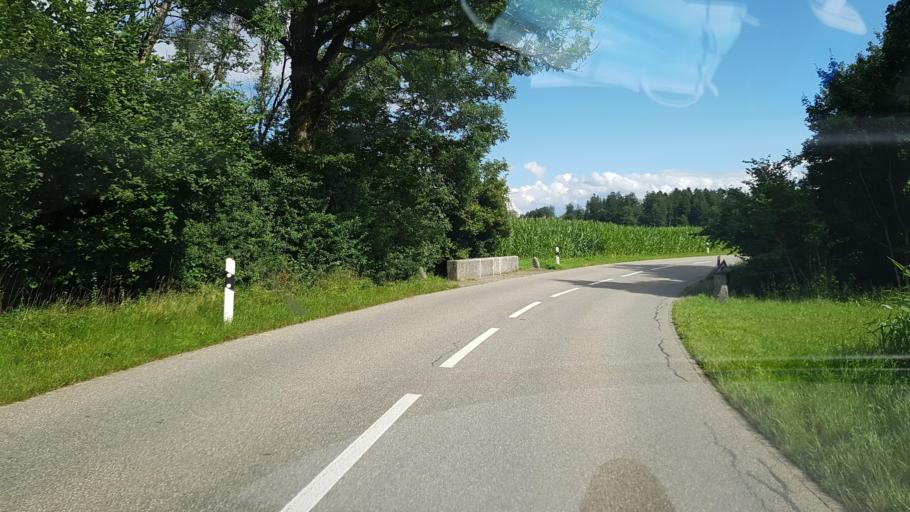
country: CH
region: Solothurn
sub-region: Bezirk Lebern
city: Riedholz
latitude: 47.2457
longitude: 7.5824
